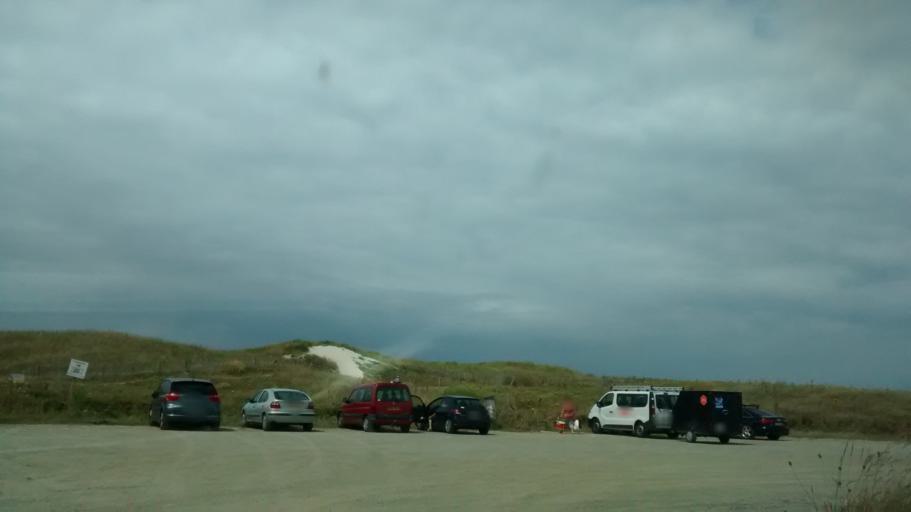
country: FR
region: Brittany
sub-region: Departement du Finistere
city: Guisseny
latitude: 48.6296
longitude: -4.4567
